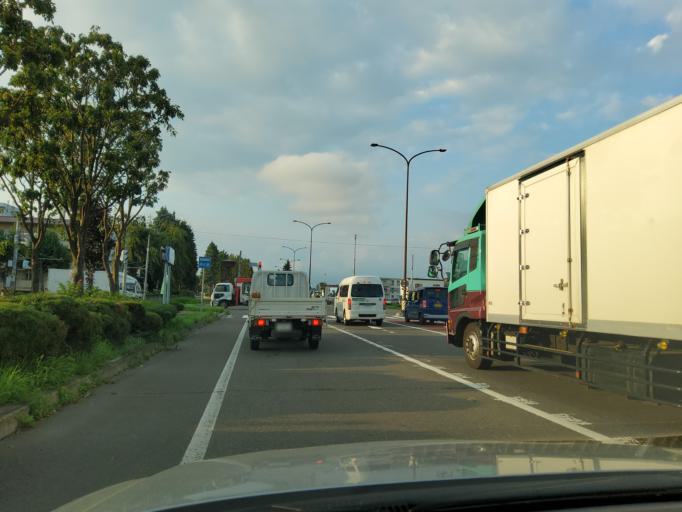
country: JP
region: Hokkaido
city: Obihiro
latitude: 42.9336
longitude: 143.1628
